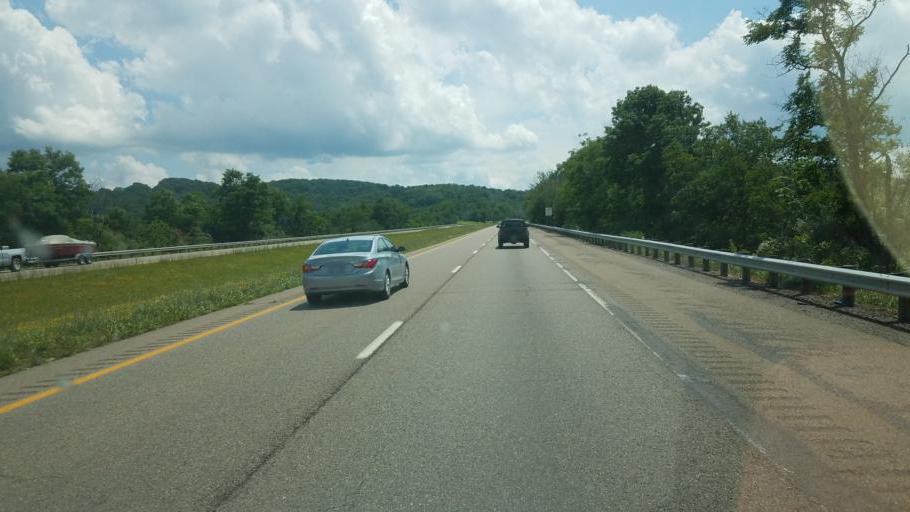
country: US
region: Ohio
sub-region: Tuscarawas County
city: New Philadelphia
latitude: 40.4181
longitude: -81.5449
